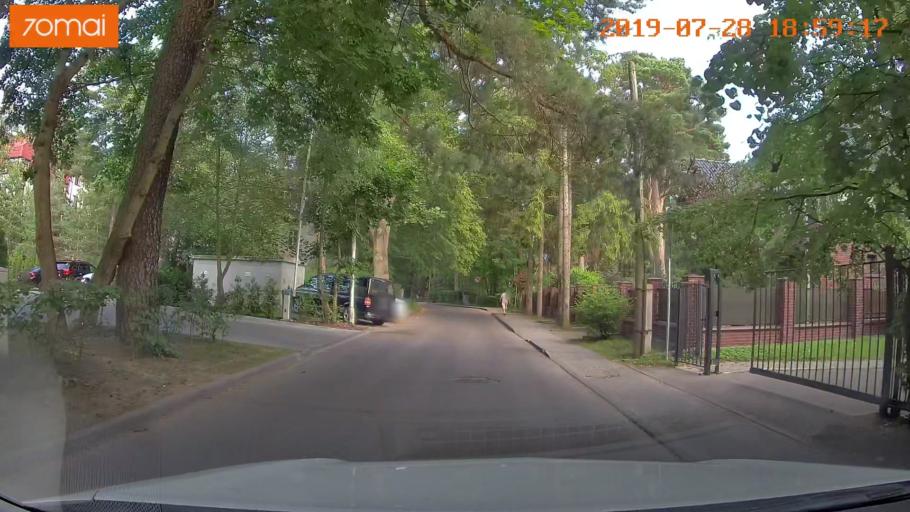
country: RU
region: Kaliningrad
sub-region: Gorod Svetlogorsk
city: Svetlogorsk
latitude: 54.9410
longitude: 20.1581
